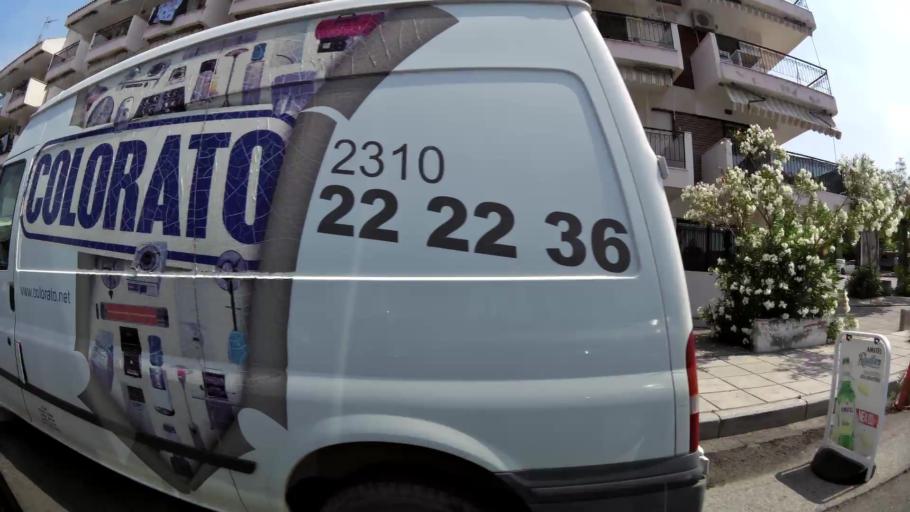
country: GR
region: Central Macedonia
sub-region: Nomos Thessalonikis
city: Agios Pavlos
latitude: 40.6274
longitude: 22.9664
